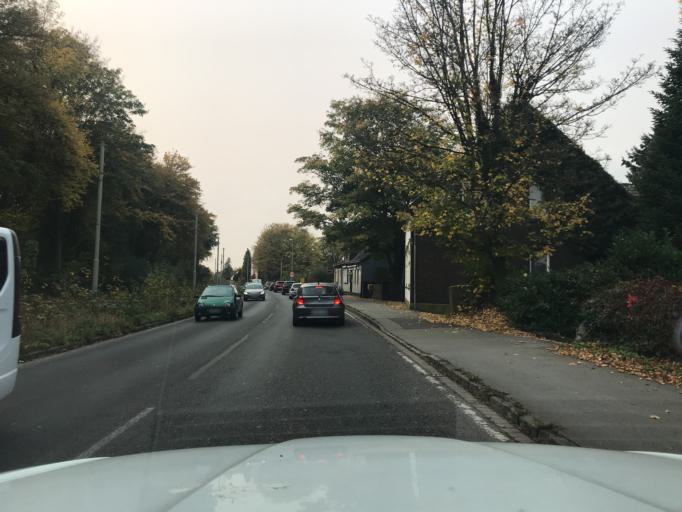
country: DE
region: North Rhine-Westphalia
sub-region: Regierungsbezirk Dusseldorf
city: Muelheim (Ruhr)
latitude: 51.4143
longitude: 6.9198
